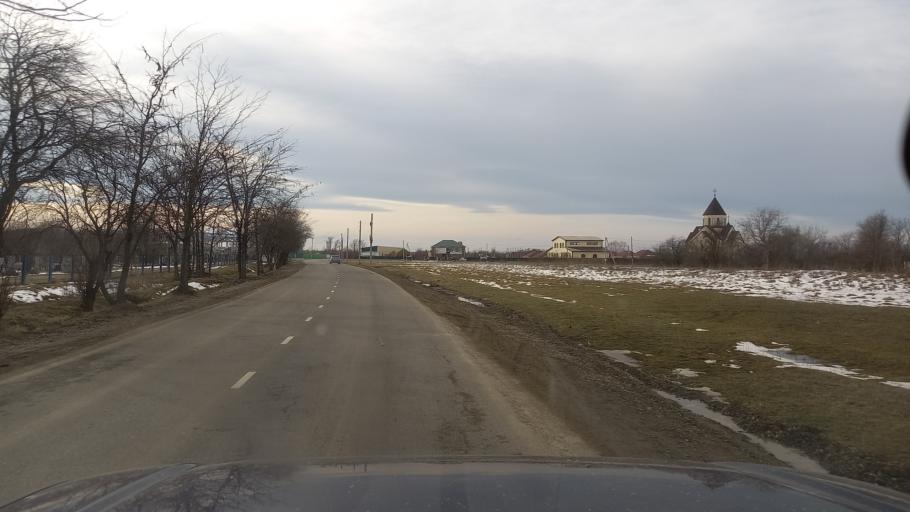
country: RU
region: Krasnodarskiy
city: Belorechensk
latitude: 44.7677
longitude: 39.9092
